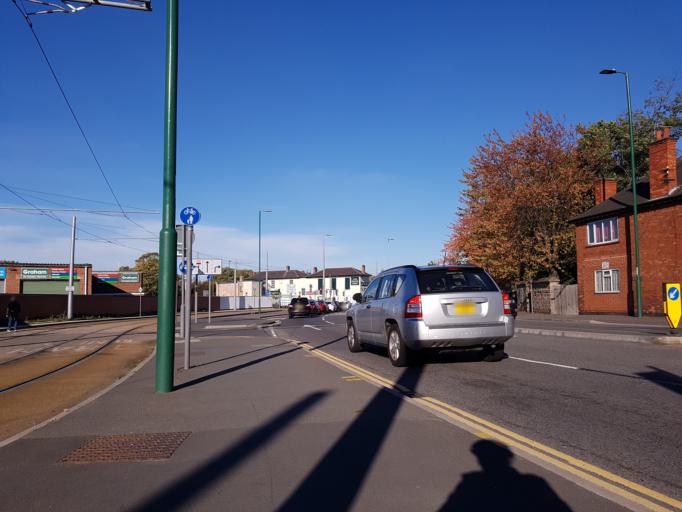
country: GB
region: England
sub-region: Nottingham
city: Nottingham
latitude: 52.9435
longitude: -1.1800
